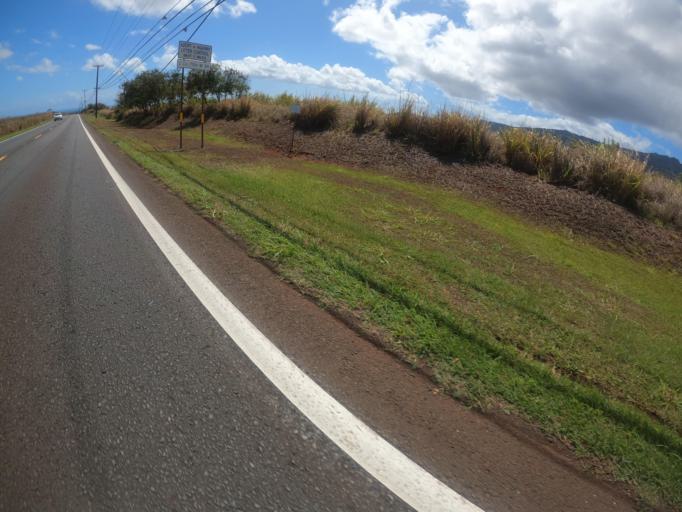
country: US
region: Hawaii
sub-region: Honolulu County
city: Village Park
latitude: 21.4126
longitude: -158.0454
